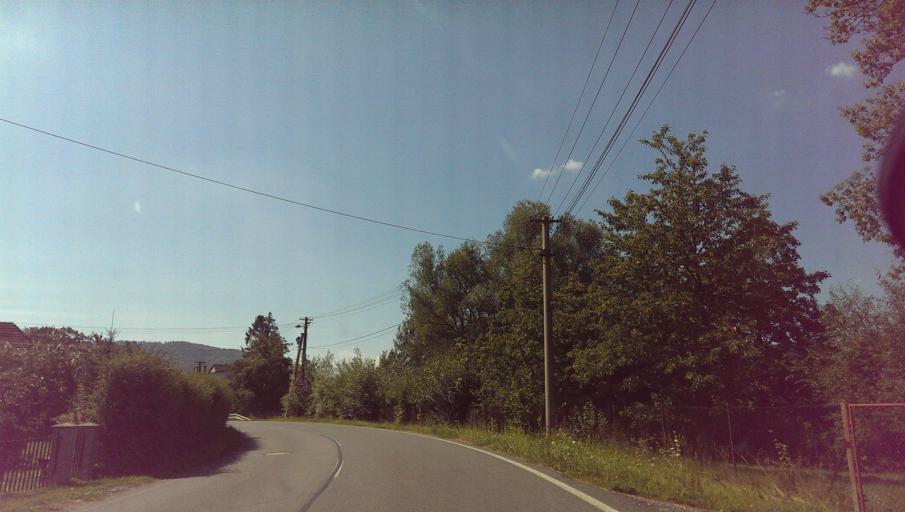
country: CZ
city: Hukvaldy
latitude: 49.6384
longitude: 18.2172
